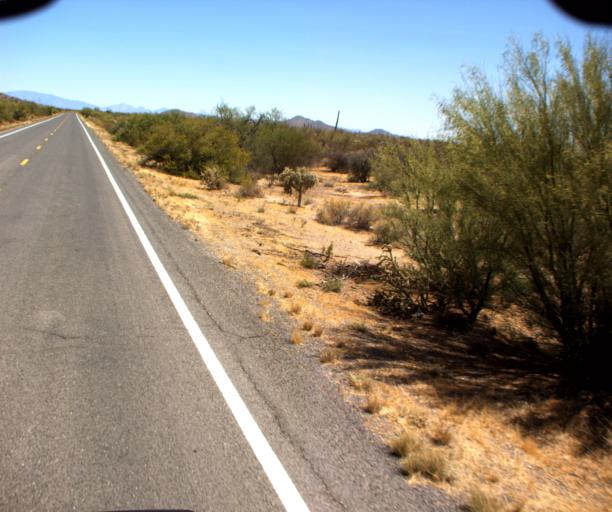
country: US
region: Arizona
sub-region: Pinal County
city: Florence
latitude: 32.7969
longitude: -111.1795
